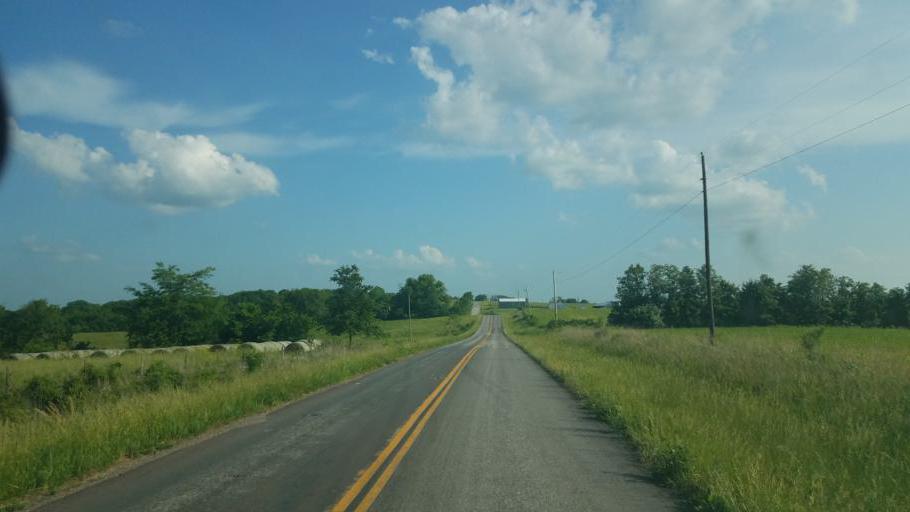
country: US
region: Missouri
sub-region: Moniteau County
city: California
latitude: 38.7684
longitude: -92.6053
